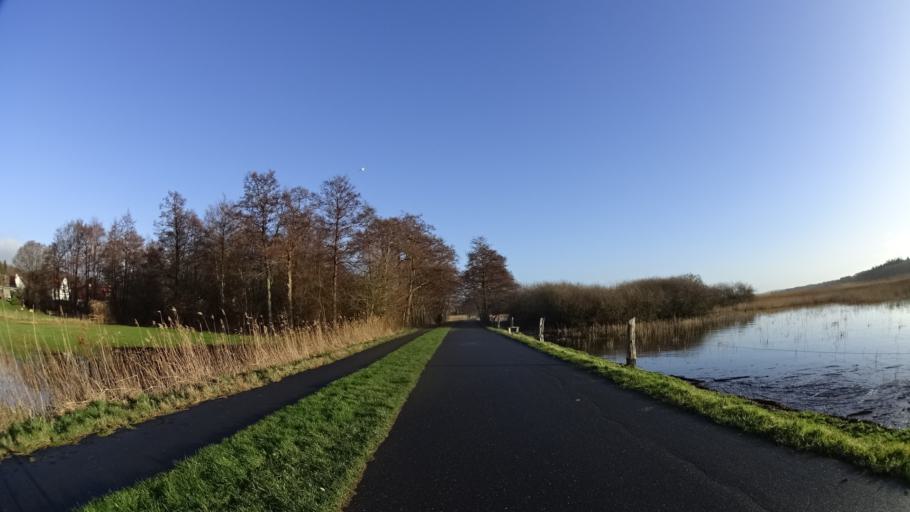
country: DK
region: Central Jutland
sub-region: Arhus Kommune
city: Stavtrup
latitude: 56.1493
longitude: 10.1142
